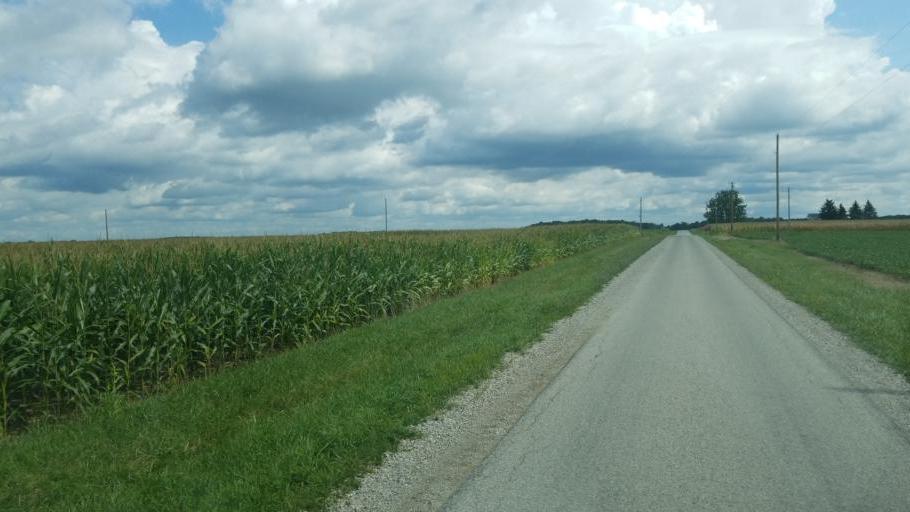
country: US
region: Ohio
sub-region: Huron County
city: Willard
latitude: 41.0953
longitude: -82.8441
